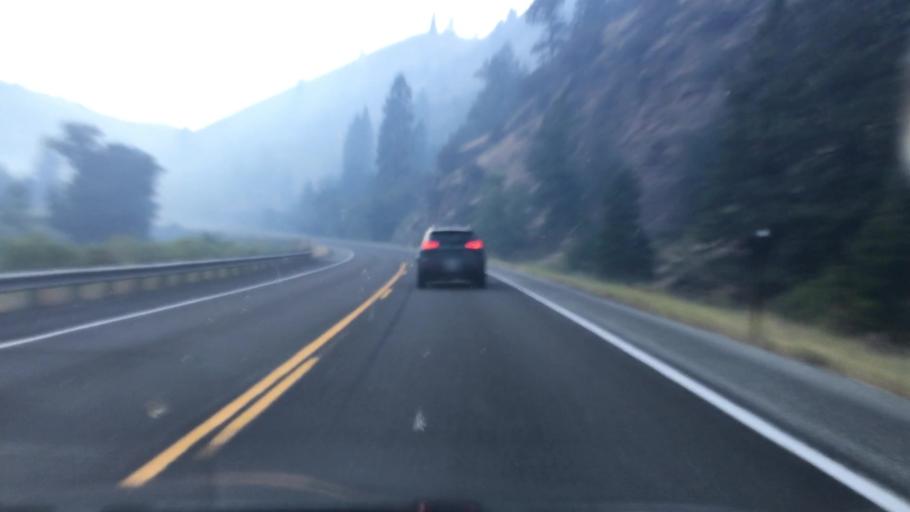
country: US
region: Idaho
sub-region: Valley County
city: McCall
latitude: 45.2805
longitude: -116.3459
